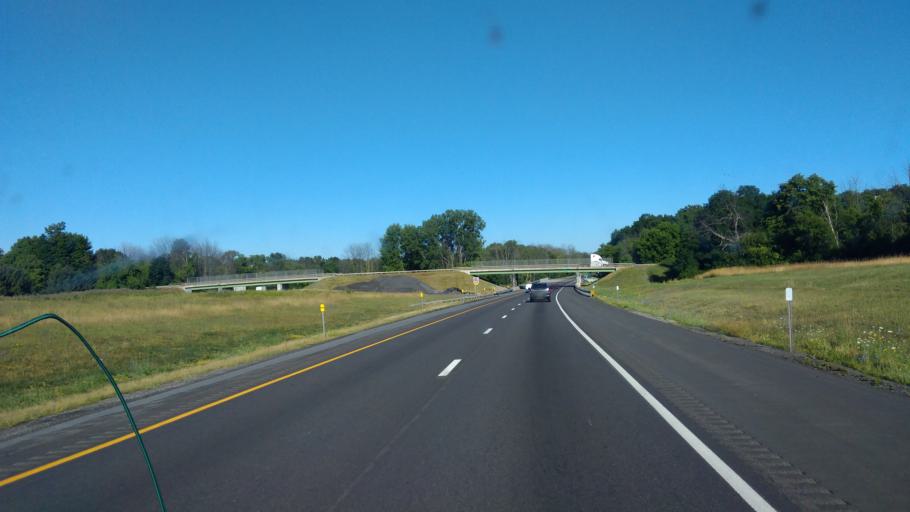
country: US
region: New York
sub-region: Ontario County
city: Clifton Springs
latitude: 42.9741
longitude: -77.1776
